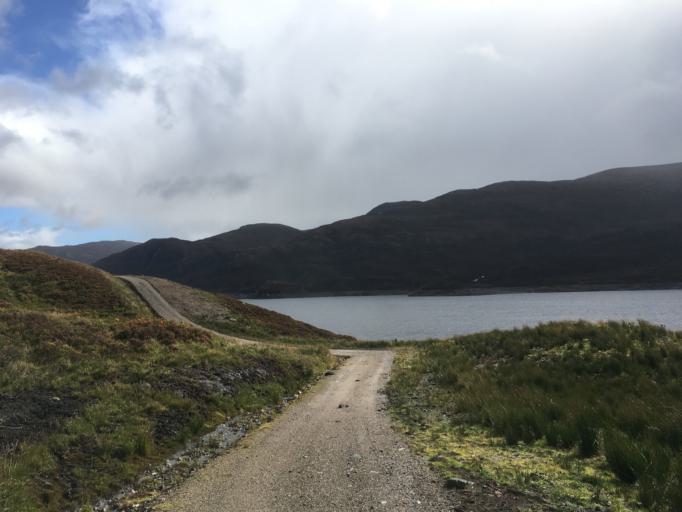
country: GB
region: Scotland
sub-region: Highland
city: Spean Bridge
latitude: 57.3414
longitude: -4.9786
